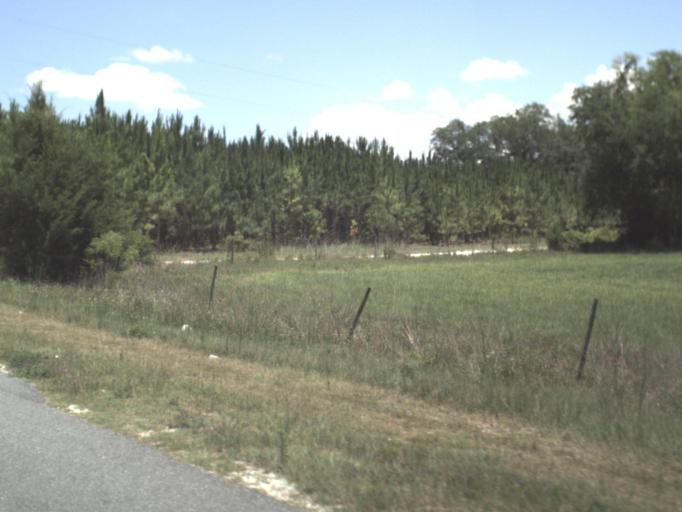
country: US
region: Florida
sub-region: Dixie County
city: Cross City
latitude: 29.7555
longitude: -82.9833
